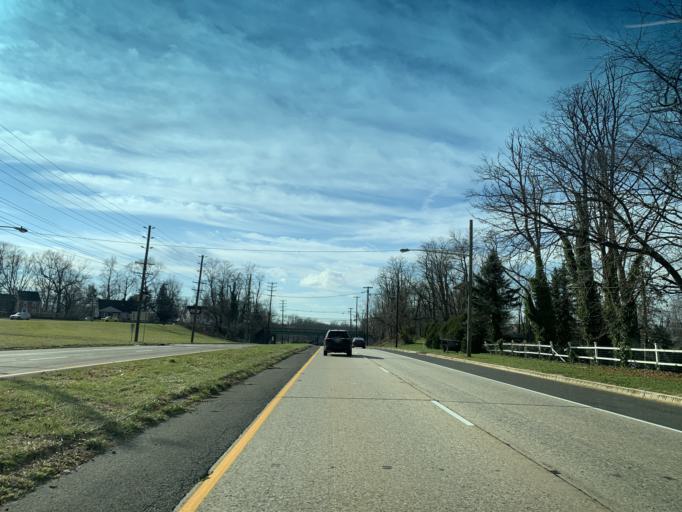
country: US
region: New Jersey
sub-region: Mercer County
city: Yardville
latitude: 40.1797
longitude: -74.6657
